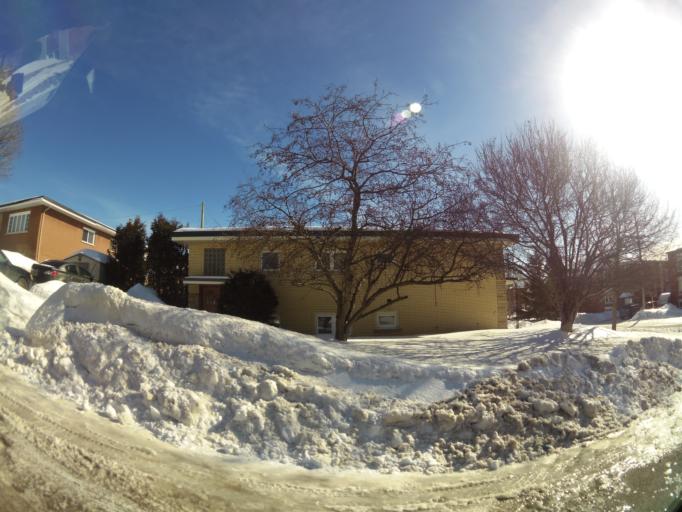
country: CA
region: Ontario
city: Ottawa
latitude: 45.4435
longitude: -75.6663
